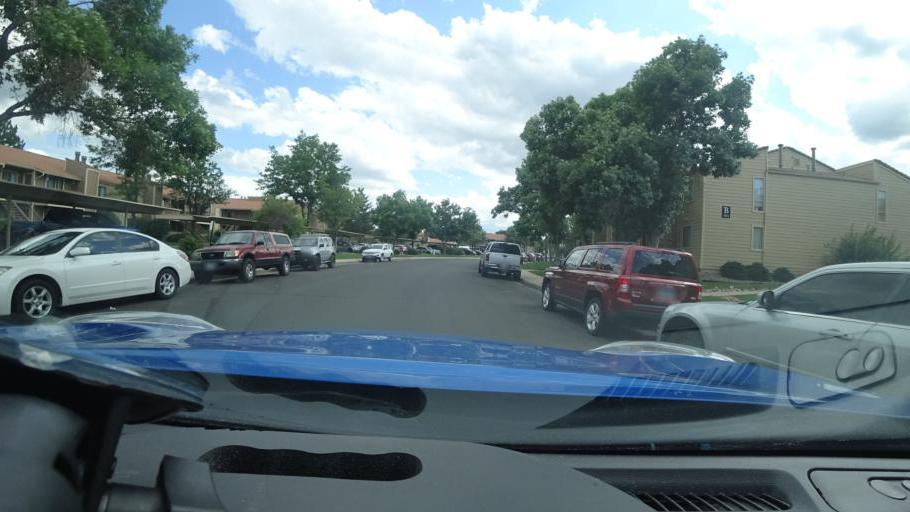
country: US
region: Colorado
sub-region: Adams County
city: Aurora
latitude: 39.6939
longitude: -104.8691
